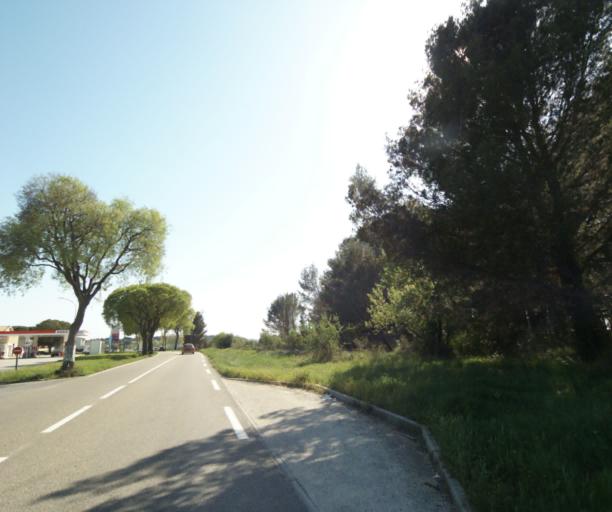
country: FR
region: Languedoc-Roussillon
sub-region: Departement de l'Herault
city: Vendargues
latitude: 43.6563
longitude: 3.9622
